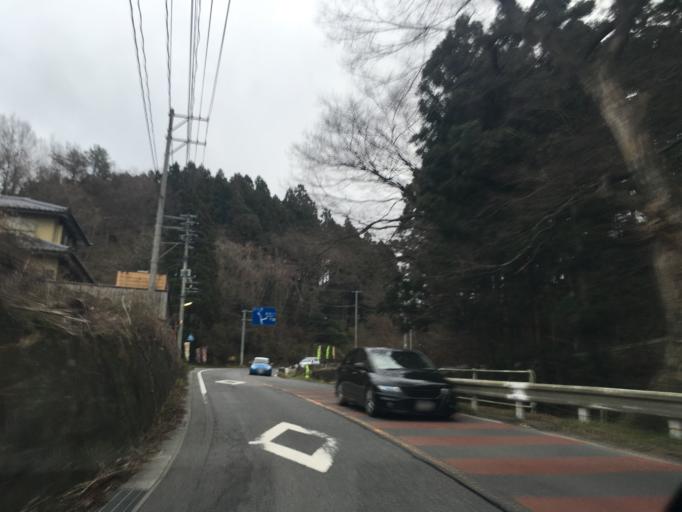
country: JP
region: Fukushima
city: Koriyama
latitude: 37.3667
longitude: 140.4478
